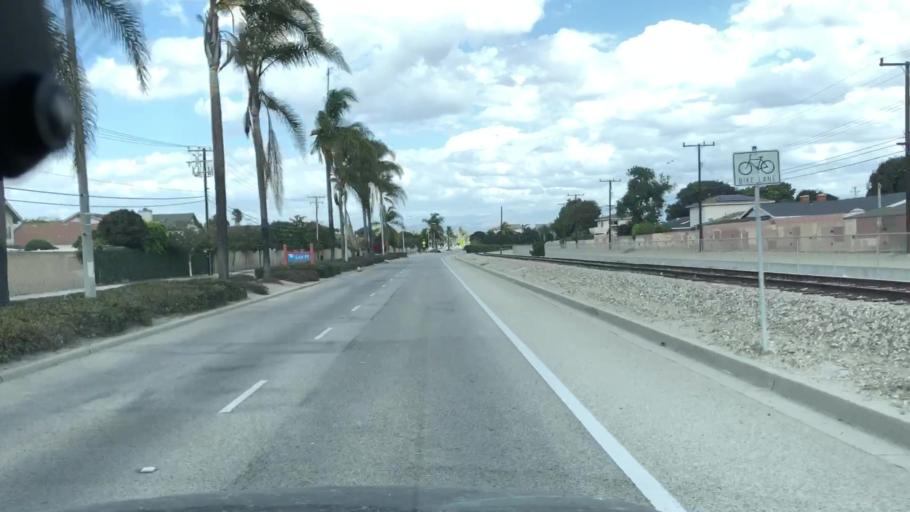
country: US
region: California
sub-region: Ventura County
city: Channel Islands Beach
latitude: 34.1839
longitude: -119.2082
